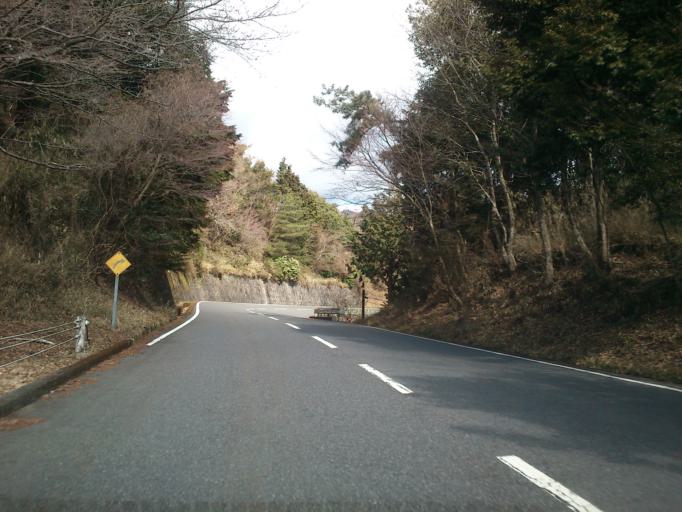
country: JP
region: Shiga Prefecture
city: Otsu-shi
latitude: 35.0395
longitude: 135.8381
